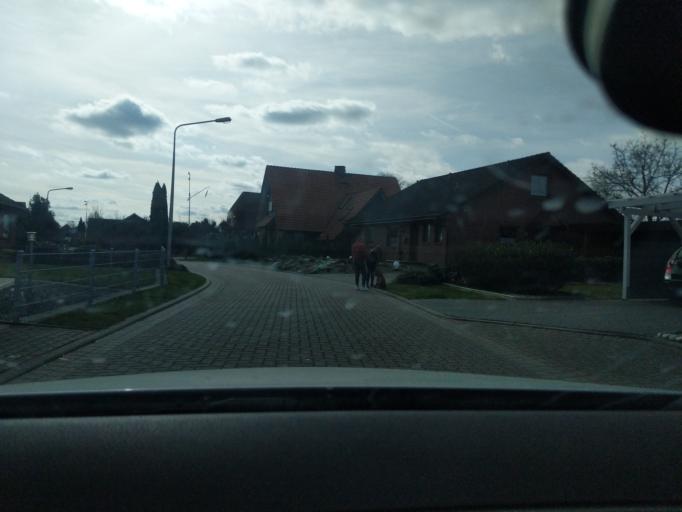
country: DE
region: Lower Saxony
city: Drochtersen
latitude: 53.6897
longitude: 9.4313
